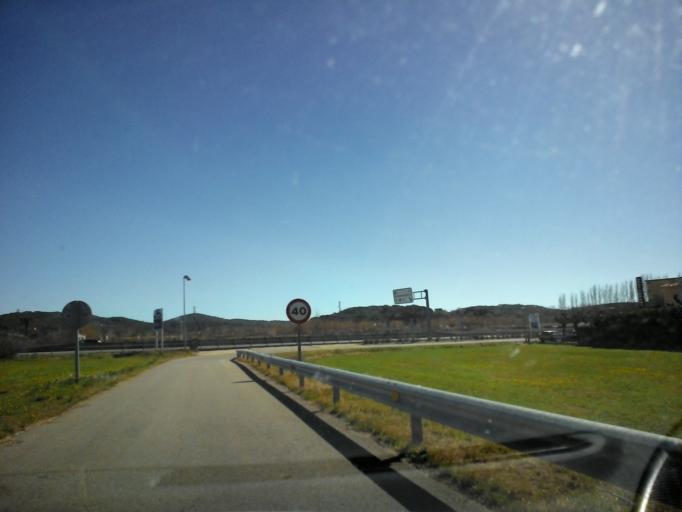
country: ES
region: Catalonia
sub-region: Provincia de Girona
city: Palamos
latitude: 41.8762
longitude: 3.1385
